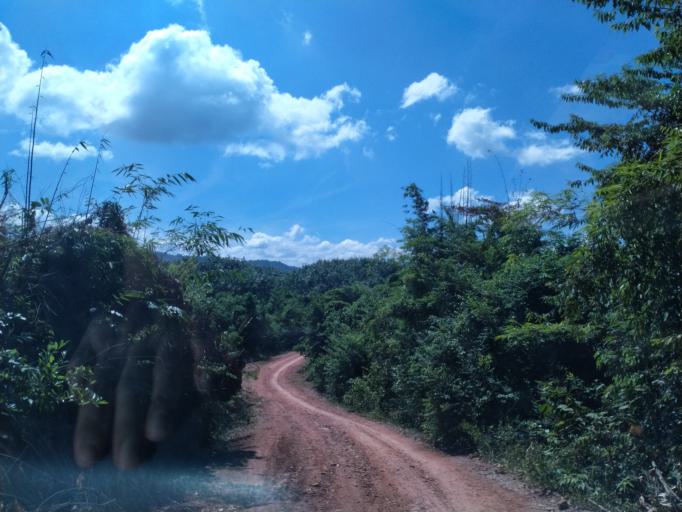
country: LA
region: Vientiane
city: Muang Phon-Hong
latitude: 18.6137
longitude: 102.8510
